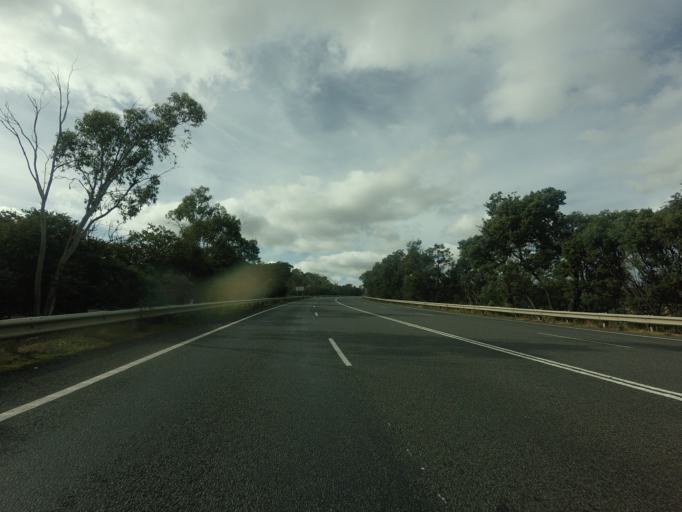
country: AU
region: Tasmania
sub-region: Brighton
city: Bridgewater
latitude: -42.4495
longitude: 147.2067
